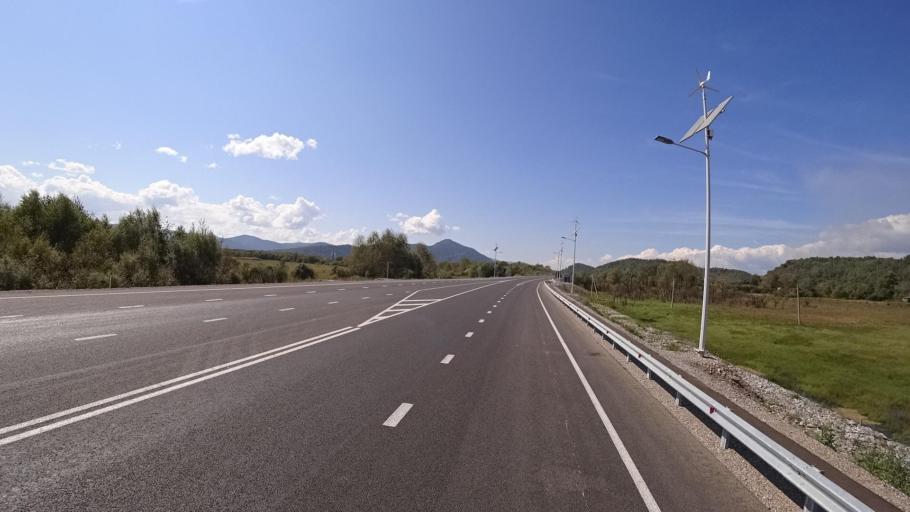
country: RU
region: Jewish Autonomous Oblast
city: Londoko
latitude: 49.0021
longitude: 131.9447
